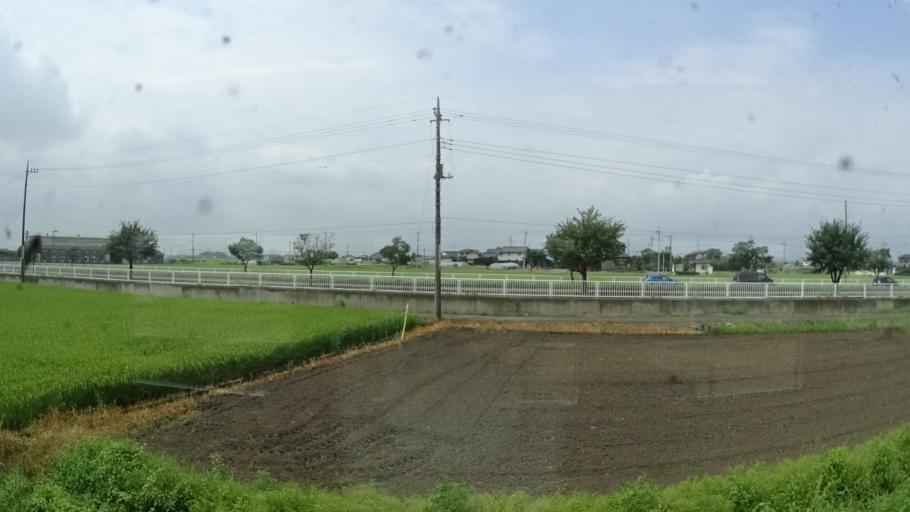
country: JP
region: Ibaraki
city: Shimodate
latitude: 36.3383
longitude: 139.9721
